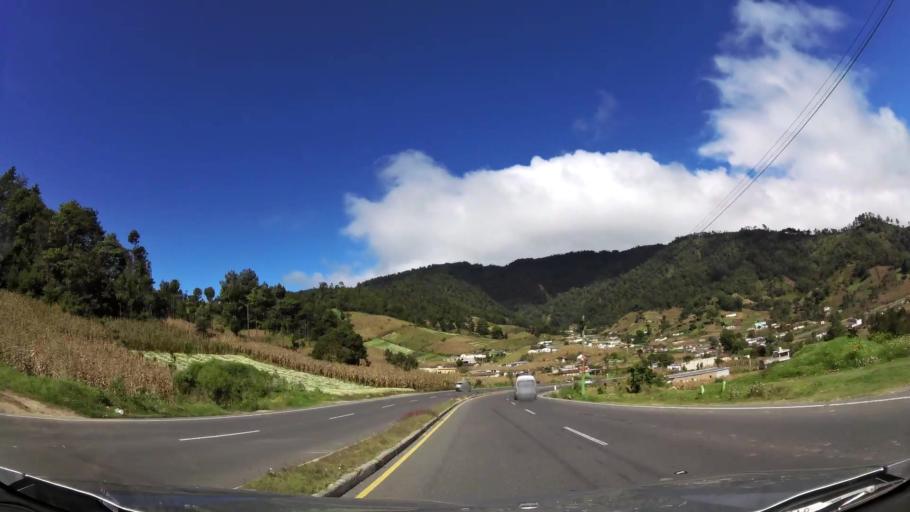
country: GT
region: Solola
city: Solola
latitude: 14.8299
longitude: -91.1842
